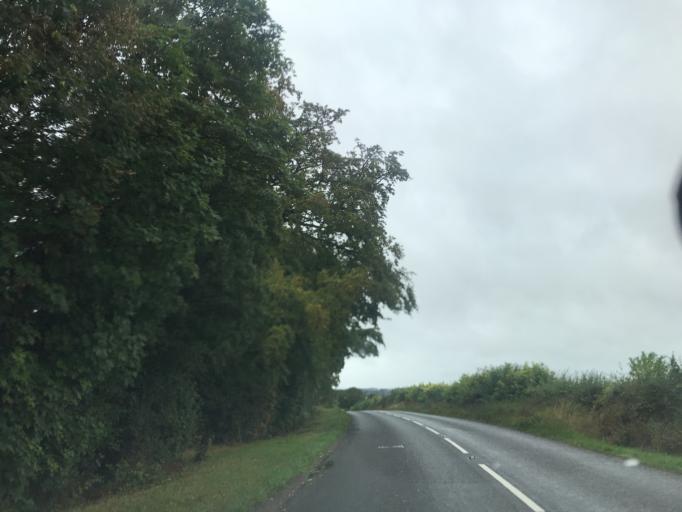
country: GB
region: England
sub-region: Buckinghamshire
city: Stone
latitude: 51.7975
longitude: -0.8556
